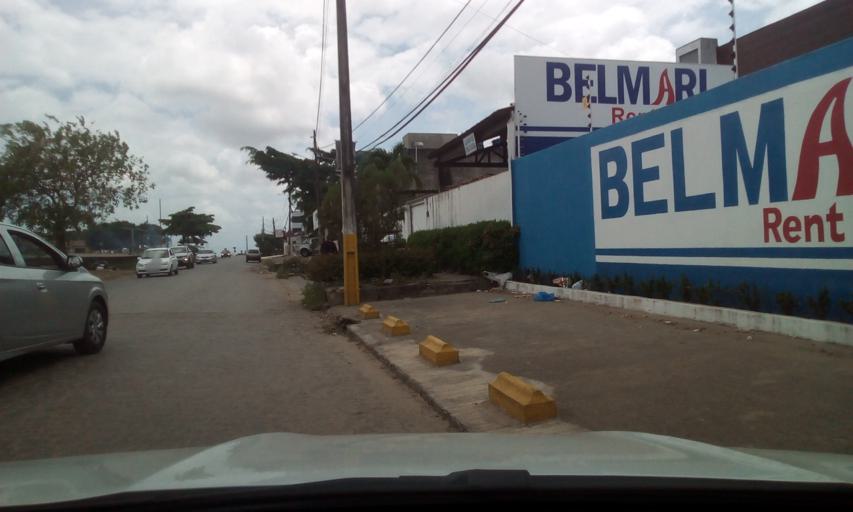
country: BR
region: Paraiba
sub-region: Bayeux
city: Bayeux
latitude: -7.1361
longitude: -34.9396
